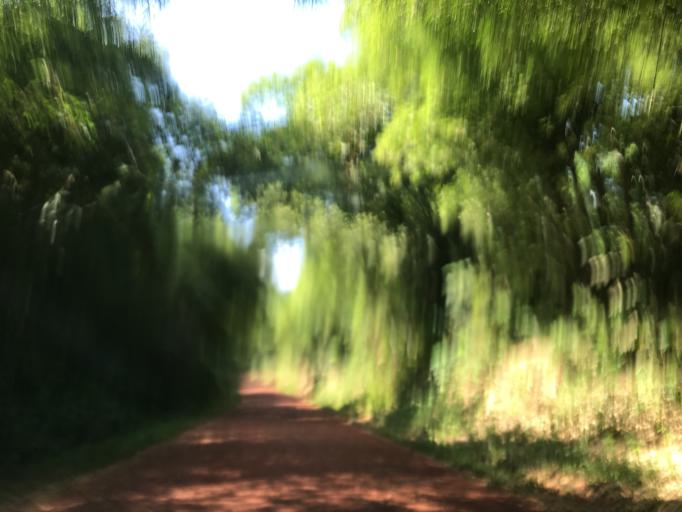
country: CD
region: Eastern Province
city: Kisangani
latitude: 1.2558
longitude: 25.2779
